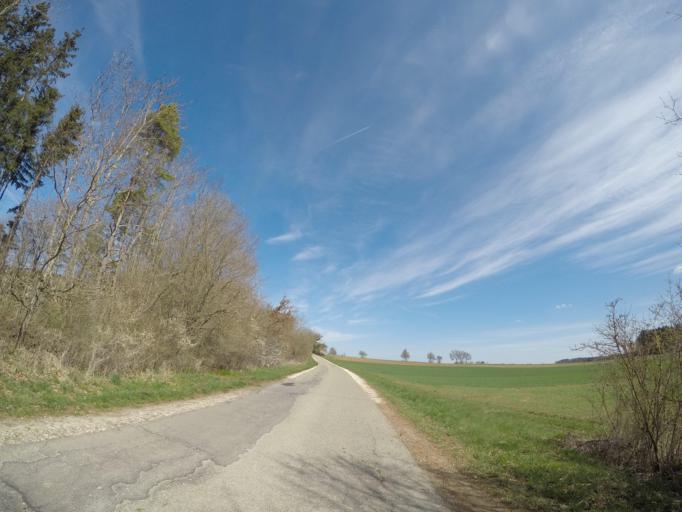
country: DE
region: Baden-Wuerttemberg
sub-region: Tuebingen Region
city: Mehrstetten
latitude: 48.3269
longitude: 9.5545
